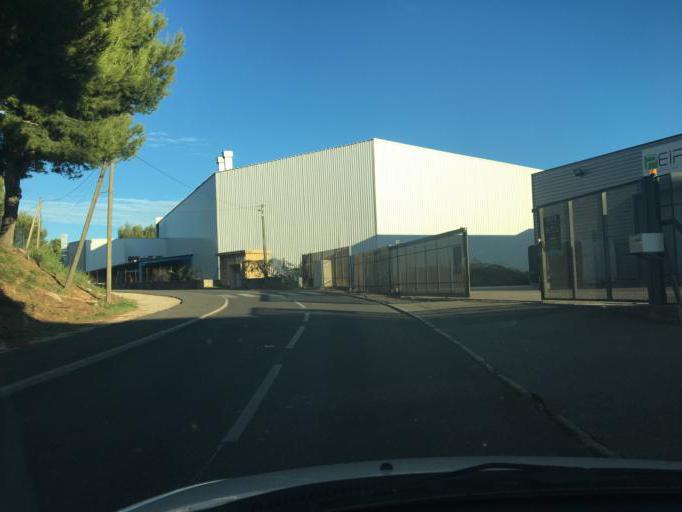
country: FR
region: Provence-Alpes-Cote d'Azur
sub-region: Departement des Bouches-du-Rhone
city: Ceyreste
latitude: 43.2047
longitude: 5.6025
